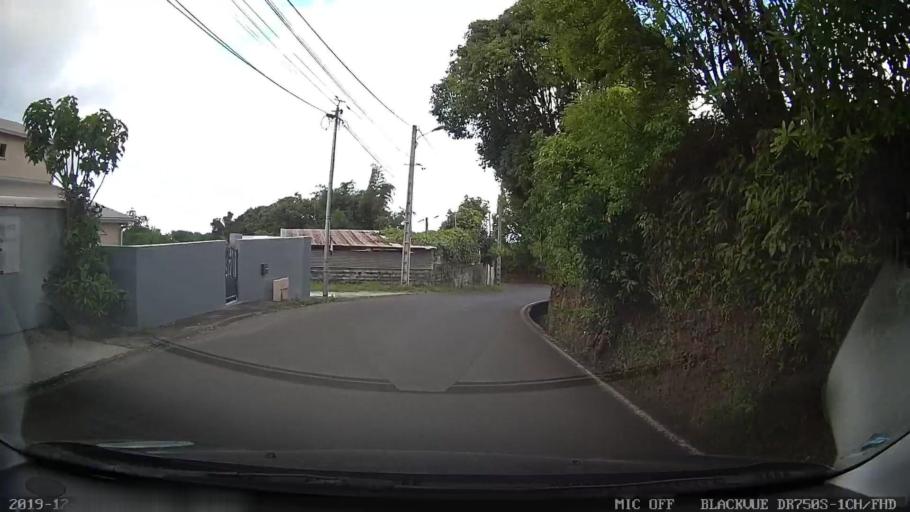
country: RE
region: Reunion
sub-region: Reunion
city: Sainte-Marie
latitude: -20.9378
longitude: 55.5339
